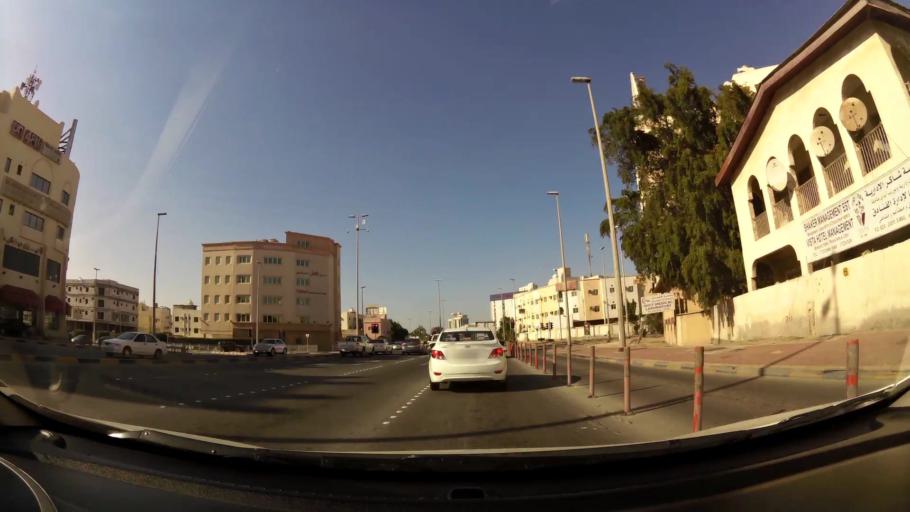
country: BH
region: Manama
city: Manama
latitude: 26.2119
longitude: 50.5661
